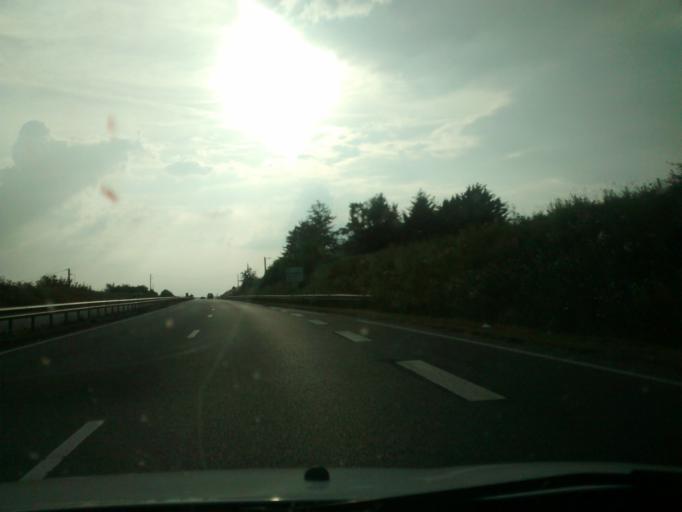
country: FR
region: Brittany
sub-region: Departement des Cotes-d'Armor
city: Rospez
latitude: 48.7167
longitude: -3.4025
